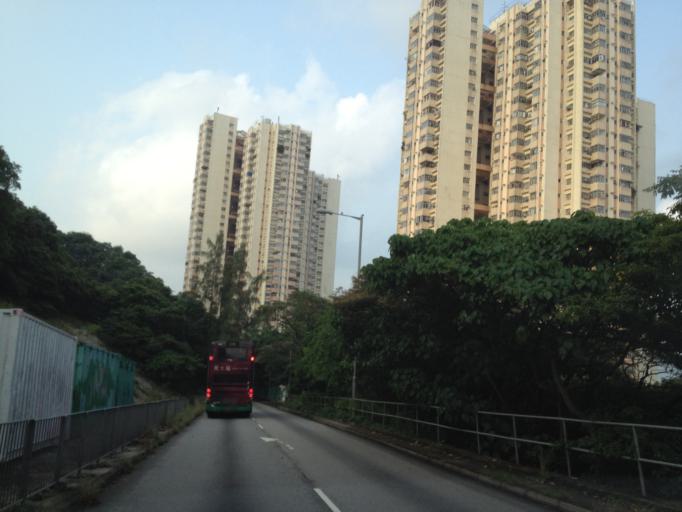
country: HK
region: Wanchai
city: Wan Chai
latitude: 22.2657
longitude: 114.2317
